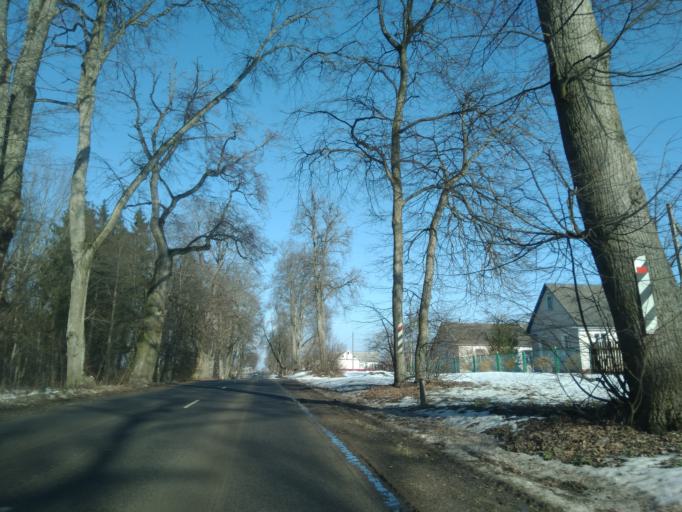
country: BY
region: Minsk
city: Nyasvizh
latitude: 53.2041
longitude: 26.6586
